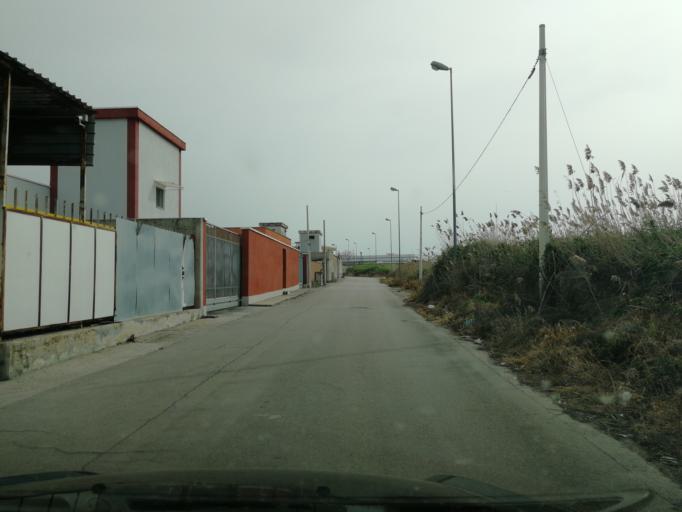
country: IT
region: Apulia
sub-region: Provincia di Barletta - Andria - Trani
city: Barletta
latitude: 41.3135
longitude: 16.3105
